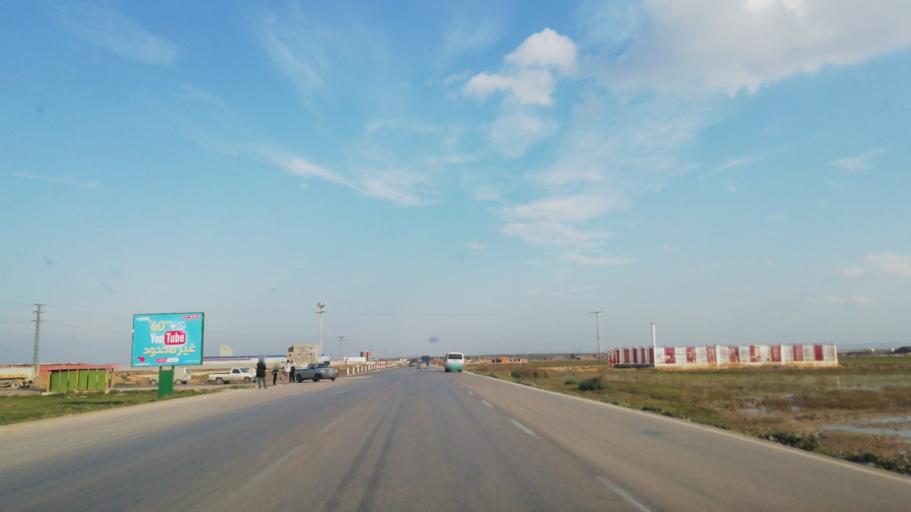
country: DZ
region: Relizane
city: Relizane
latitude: 35.8978
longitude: 0.5721
